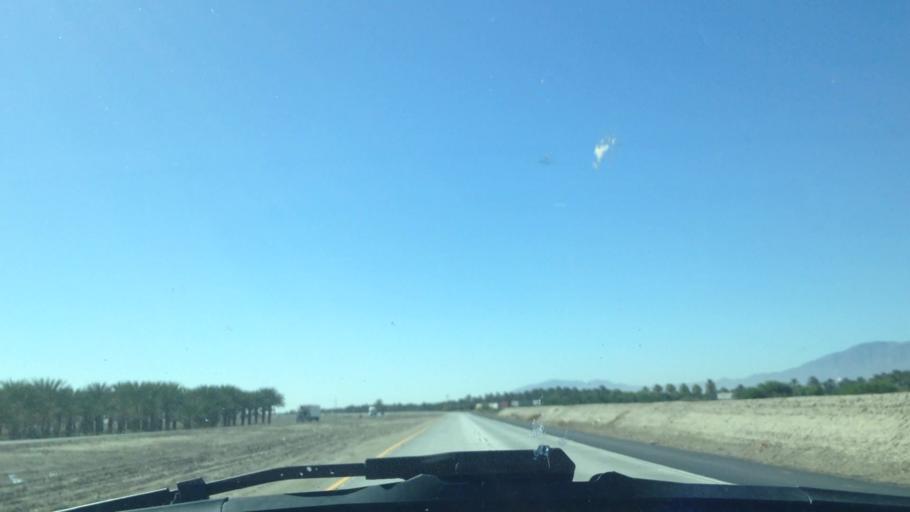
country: US
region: California
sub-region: Riverside County
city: Thermal
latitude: 33.6263
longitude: -116.1223
